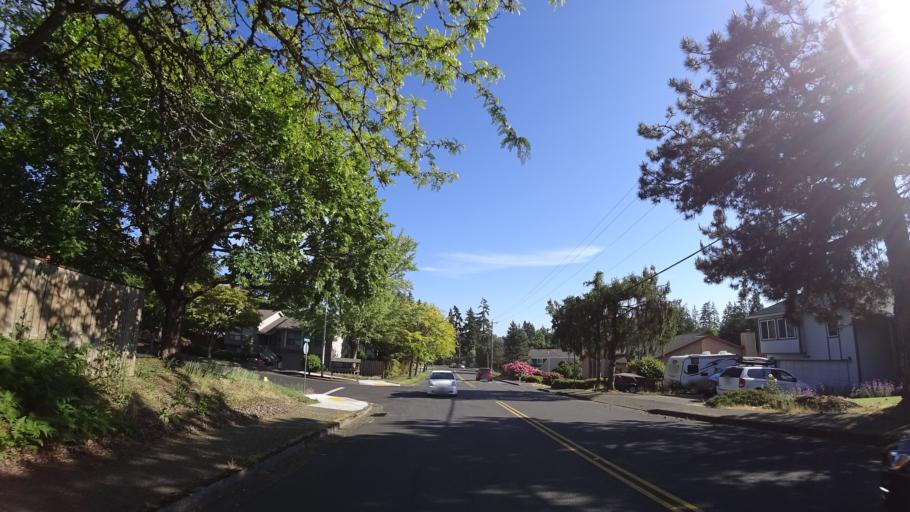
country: US
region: Oregon
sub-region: Washington County
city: Beaverton
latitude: 45.4562
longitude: -122.8080
